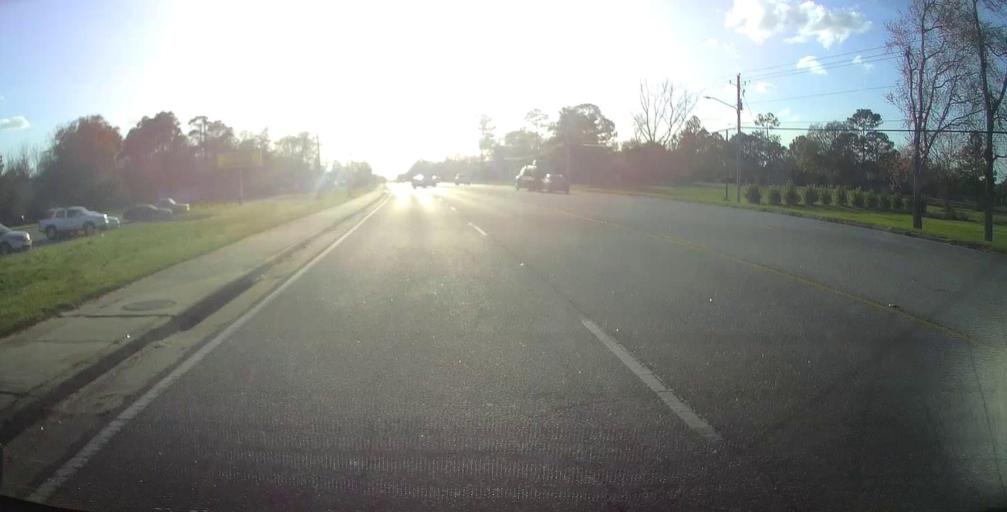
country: US
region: Georgia
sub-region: Evans County
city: Claxton
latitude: 32.1596
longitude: -81.9304
